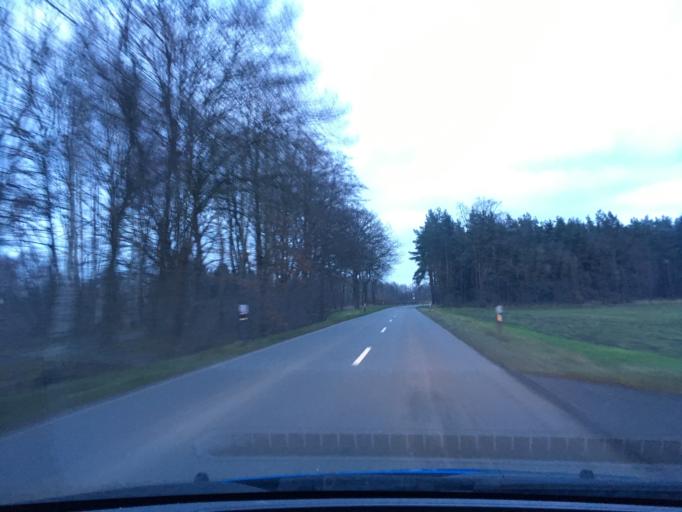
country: DE
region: Lower Saxony
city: Vogelsen
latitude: 53.3013
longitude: 10.3366
